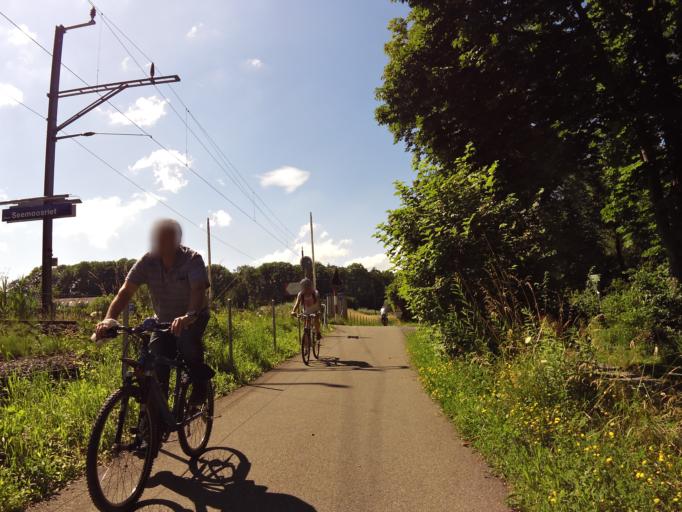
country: CH
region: Thurgau
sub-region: Arbon District
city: Arbon
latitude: 47.5217
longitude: 9.4241
